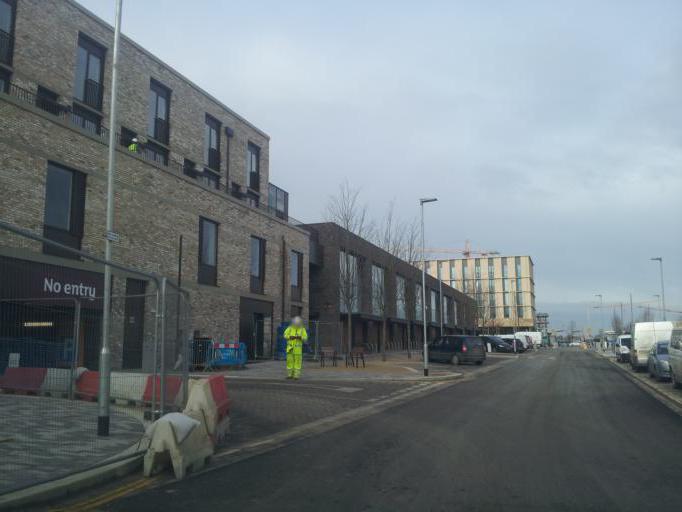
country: GB
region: England
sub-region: Cambridgeshire
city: Girton
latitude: 52.2172
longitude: 0.0881
